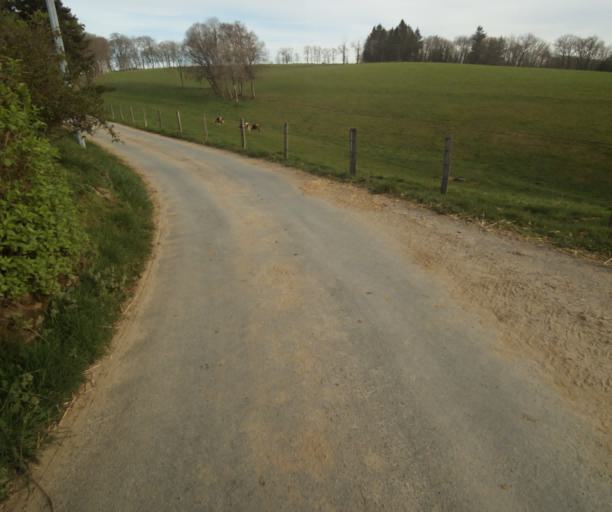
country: FR
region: Limousin
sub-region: Departement de la Correze
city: Chamboulive
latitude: 45.4509
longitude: 1.7575
